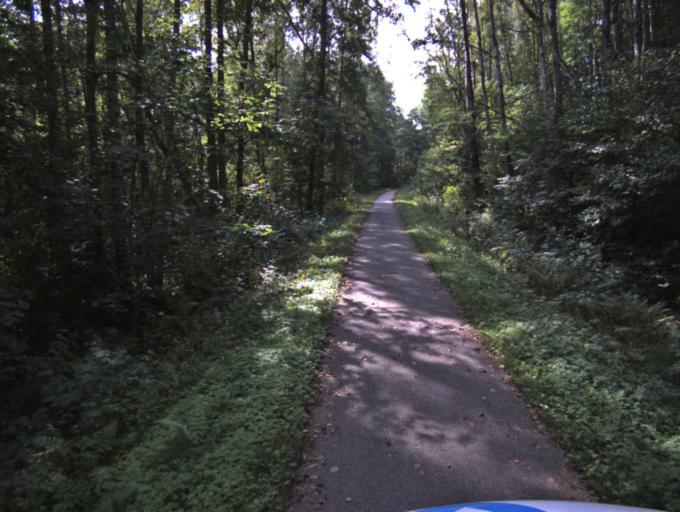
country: SE
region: Vaestra Goetaland
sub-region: Tranemo Kommun
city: Limmared
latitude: 57.6442
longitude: 13.3594
